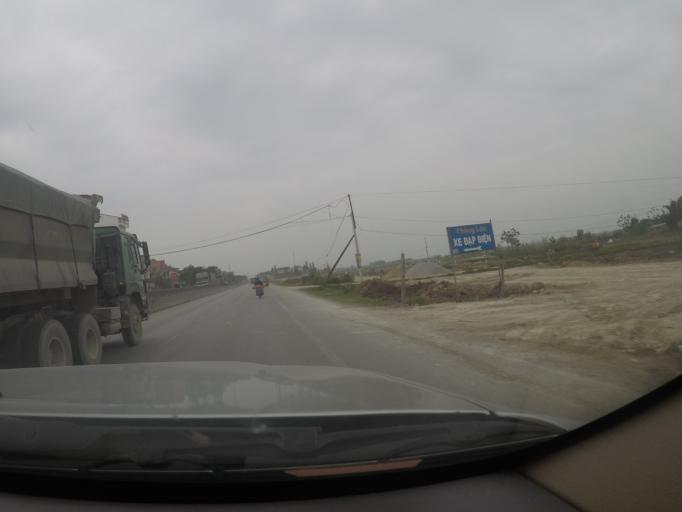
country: VN
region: Nghe An
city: Dien Chau
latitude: 19.0529
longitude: 105.5823
